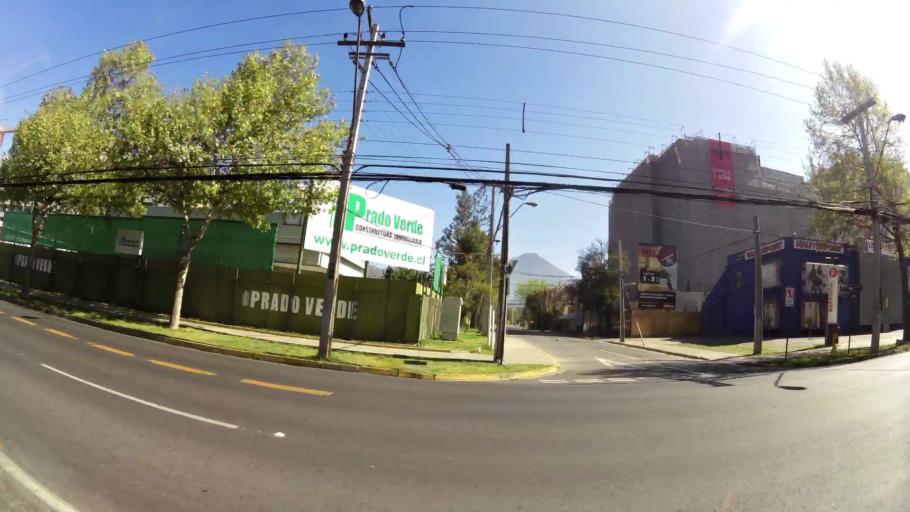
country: CL
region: Santiago Metropolitan
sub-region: Provincia de Santiago
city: Villa Presidente Frei, Nunoa, Santiago, Chile
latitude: -33.3955
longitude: -70.5487
